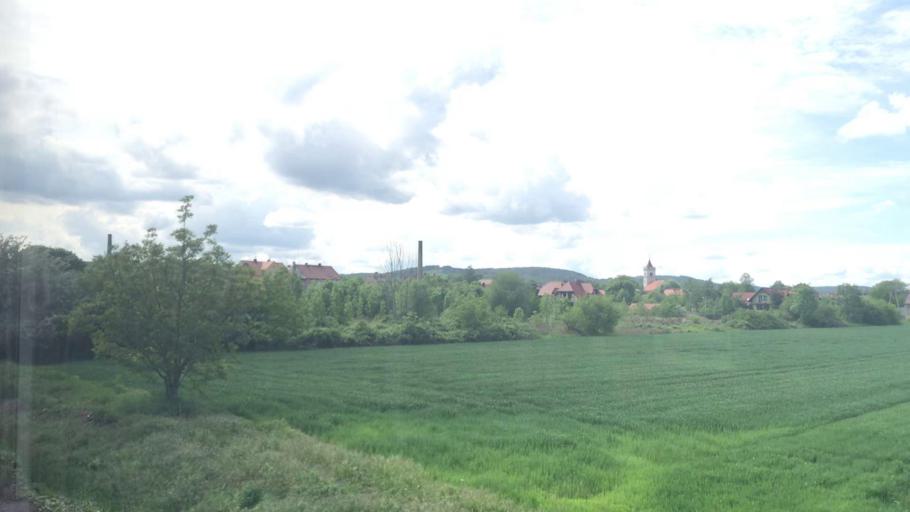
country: PL
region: Lower Silesian Voivodeship
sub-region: Powiat swidnicki
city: Swiebodzice
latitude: 50.8643
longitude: 16.3317
